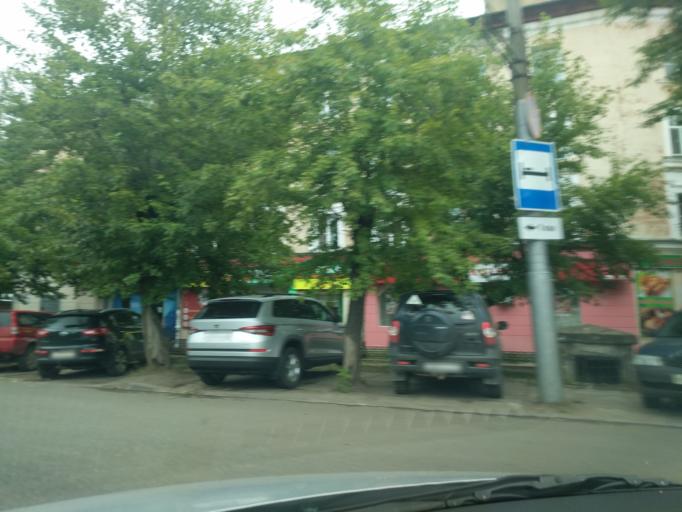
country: RU
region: Kirov
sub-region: Kirovo-Chepetskiy Rayon
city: Kirov
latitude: 58.6368
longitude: 49.6131
